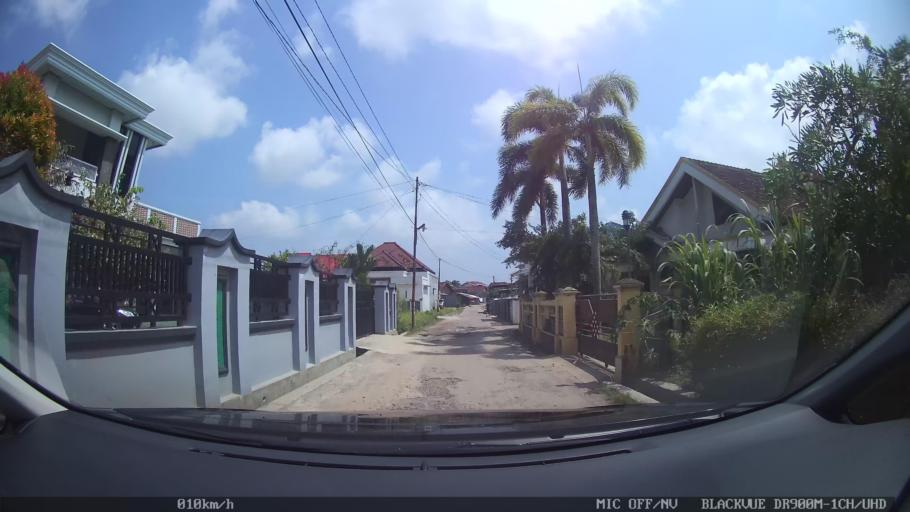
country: ID
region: Lampung
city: Kedaton
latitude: -5.3574
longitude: 105.2845
